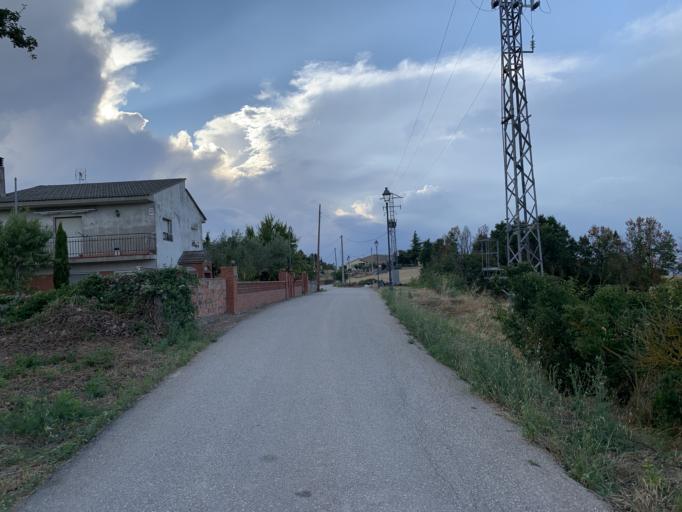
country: ES
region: Catalonia
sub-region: Provincia de Tarragona
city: Vallfogona de Riucorb
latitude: 41.5431
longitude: 1.2690
